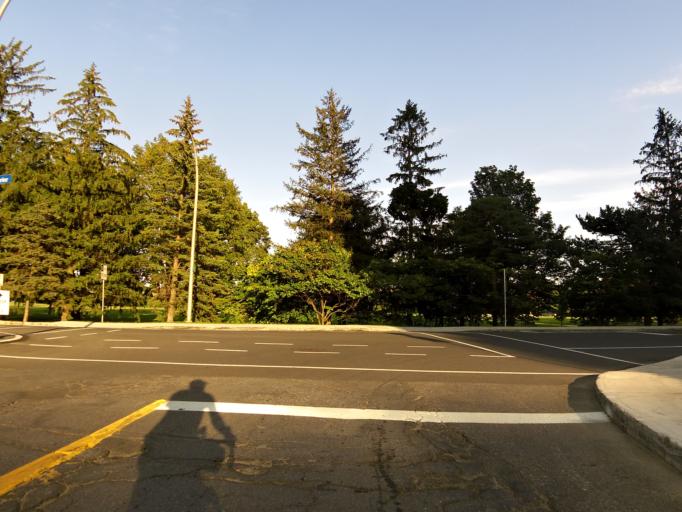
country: CA
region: Ontario
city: Ottawa
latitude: 45.4404
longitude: -75.7083
